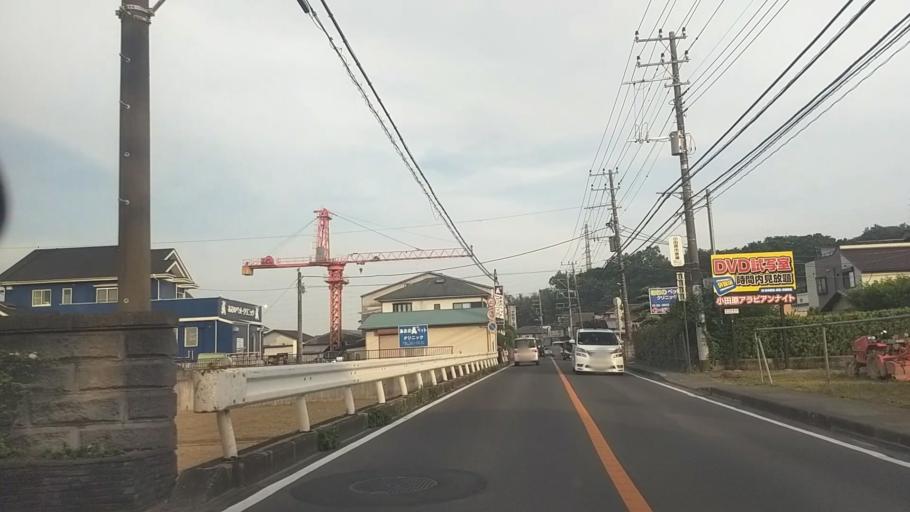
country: JP
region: Kanagawa
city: Odawara
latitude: 35.2852
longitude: 139.1410
